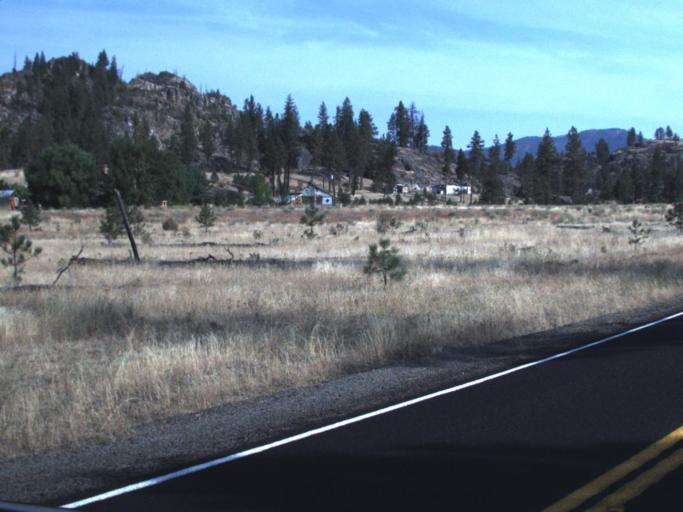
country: US
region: Washington
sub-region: Spokane County
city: Airway Heights
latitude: 47.8528
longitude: -117.7137
